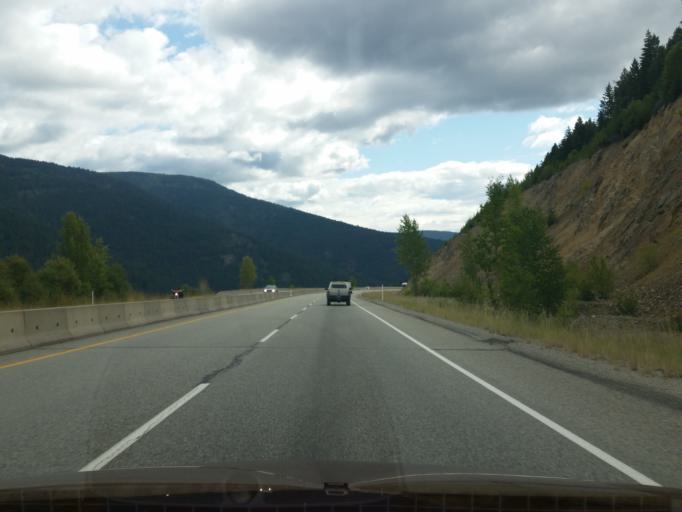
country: CA
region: British Columbia
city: Peachland
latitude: 49.8639
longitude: -119.8648
